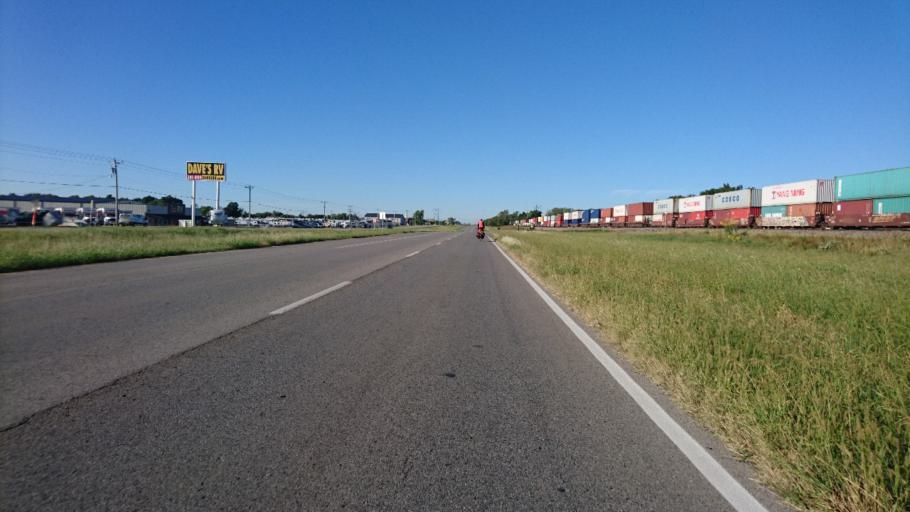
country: US
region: Oklahoma
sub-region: Rogers County
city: Verdigris
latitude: 36.2600
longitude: -95.6576
